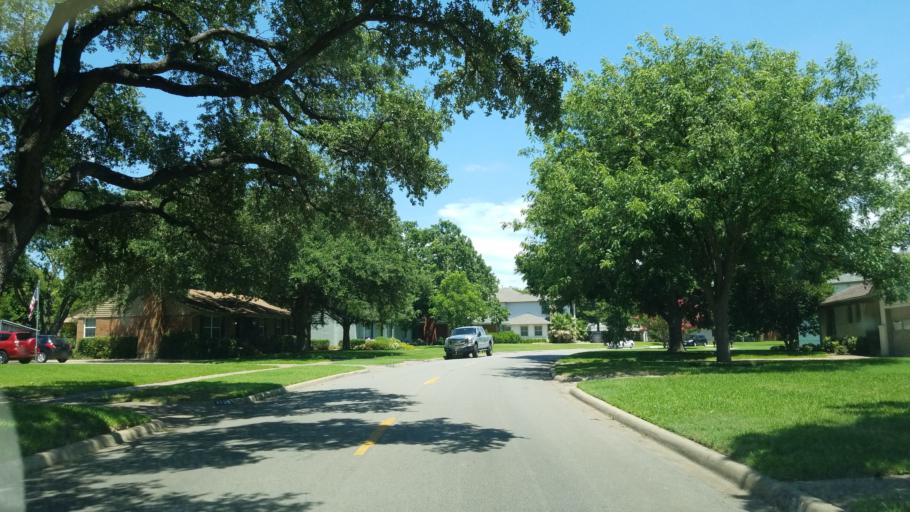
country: US
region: Texas
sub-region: Dallas County
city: University Park
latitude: 32.8753
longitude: -96.8412
